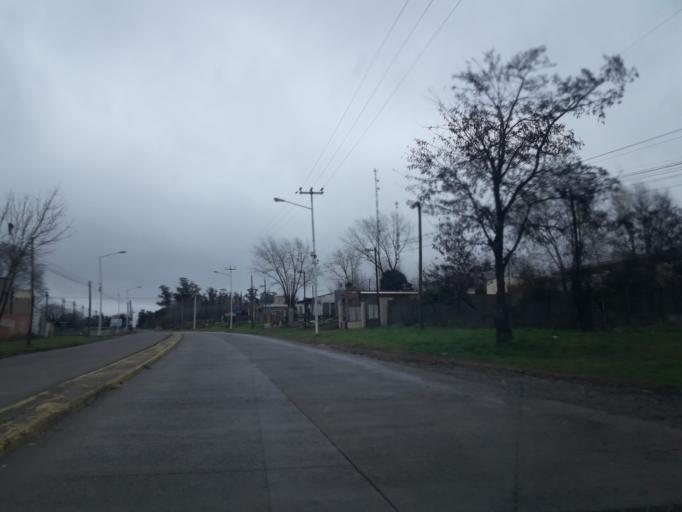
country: AR
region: Buenos Aires
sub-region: Partido de Tandil
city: Tandil
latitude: -37.3244
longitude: -59.1704
